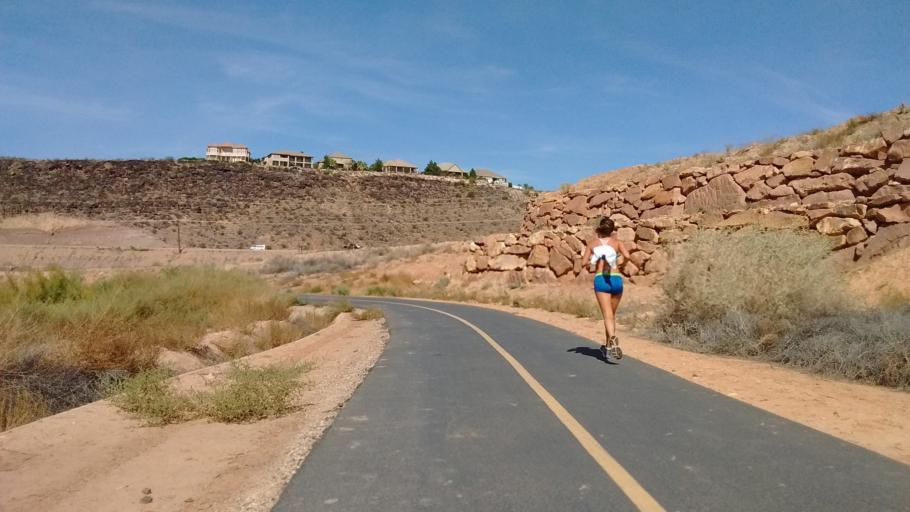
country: US
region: Utah
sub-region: Washington County
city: Saint George
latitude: 37.0866
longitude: -113.5446
